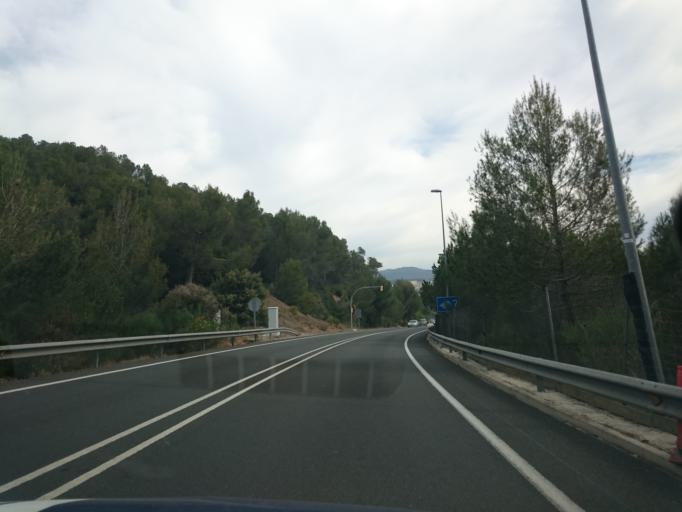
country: ES
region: Catalonia
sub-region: Provincia de Barcelona
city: Capellades
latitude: 41.5064
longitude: 1.7008
